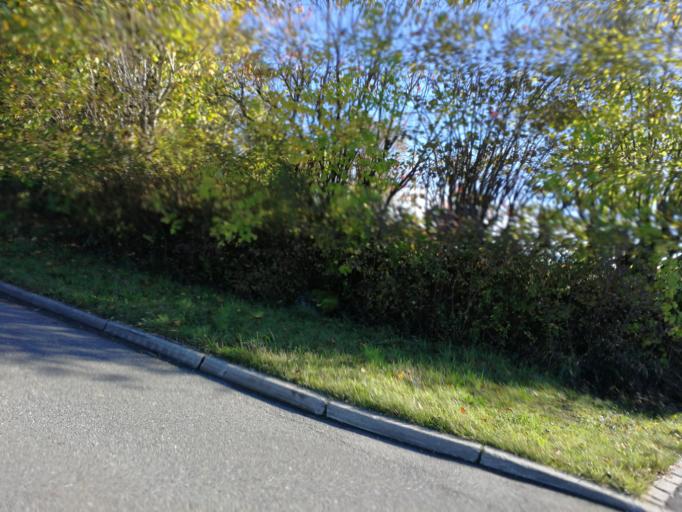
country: CH
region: Zurich
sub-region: Bezirk Uster
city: Moenchaltorf / Dorf
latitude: 47.2900
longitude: 8.7326
